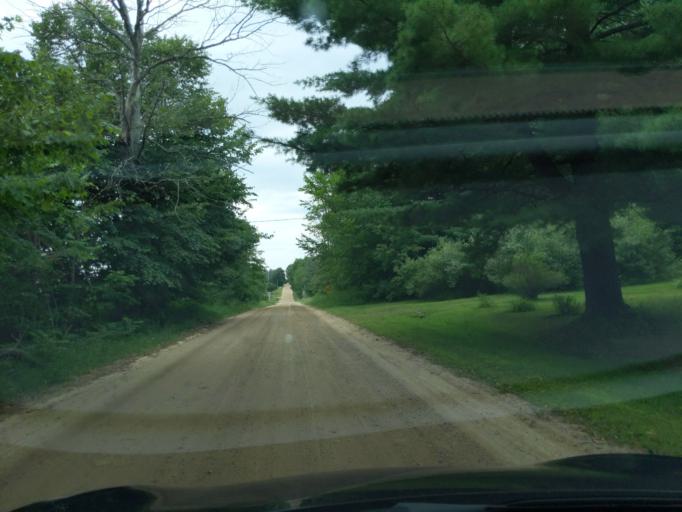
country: US
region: Michigan
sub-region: Clare County
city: Harrison
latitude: 44.0025
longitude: -84.9722
